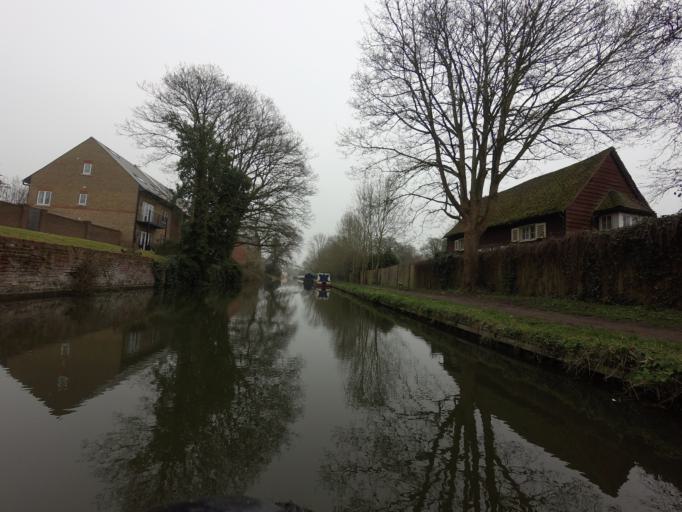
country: GB
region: England
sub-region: Hertfordshire
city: Berkhamsted
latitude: 51.7567
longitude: -0.5486
